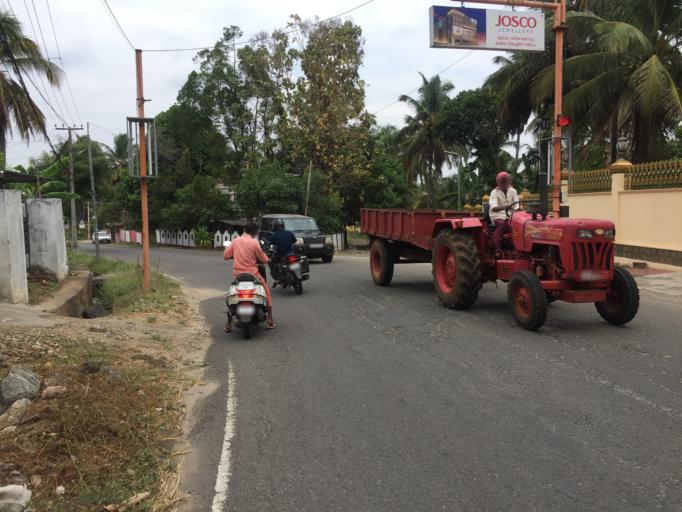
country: IN
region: Kerala
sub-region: Palakkad district
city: Chittur
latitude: 10.6845
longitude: 76.7150
